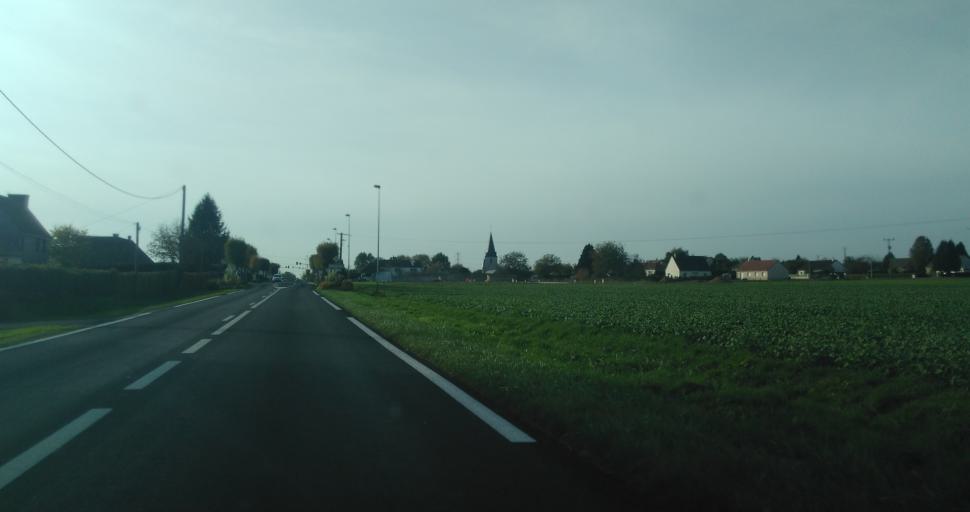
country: FR
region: Haute-Normandie
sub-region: Departement de l'Eure
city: Hauville
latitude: 49.3581
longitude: 0.7271
